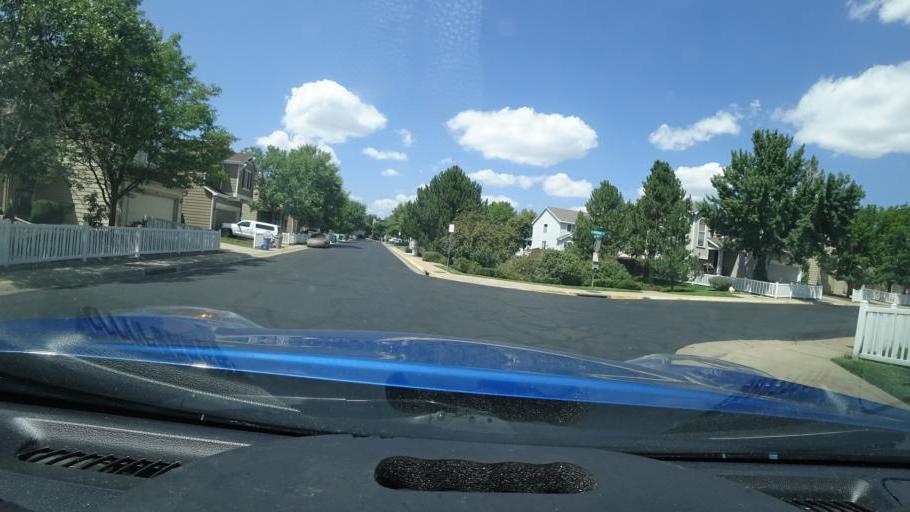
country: US
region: Colorado
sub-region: Arapahoe County
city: Glendale
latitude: 39.6932
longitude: -104.8779
